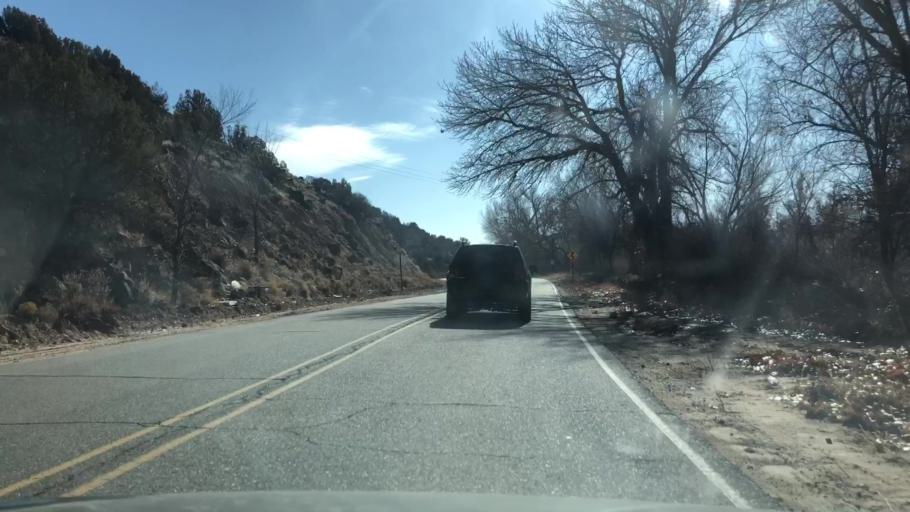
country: US
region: New Mexico
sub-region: Rio Arriba County
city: Ohkay Owingeh
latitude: 36.0877
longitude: -106.1282
